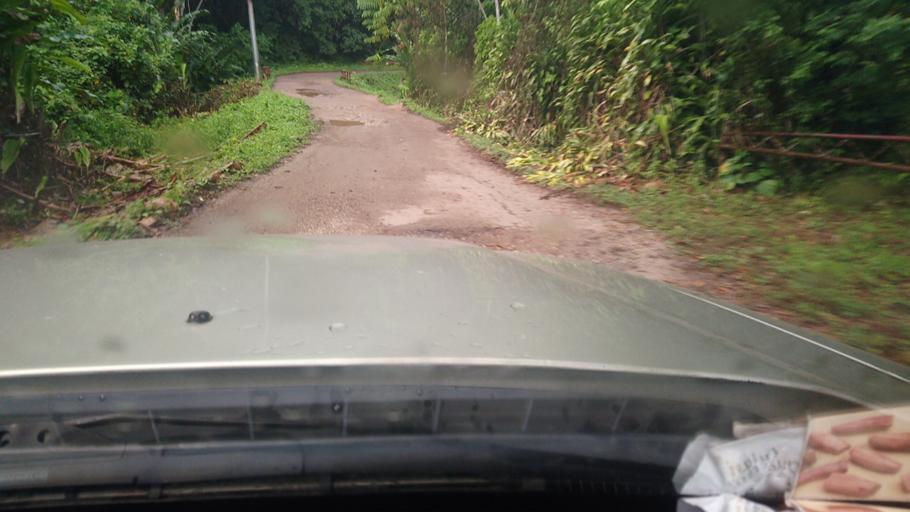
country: TT
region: Couva-Tabaquite-Talparo
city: Tabaquite
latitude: 10.4816
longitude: -61.2094
